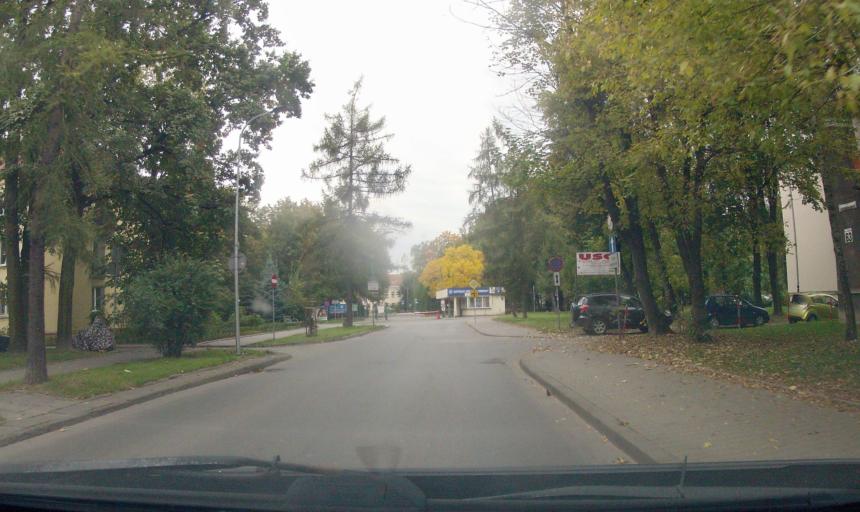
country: PL
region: Lesser Poland Voivodeship
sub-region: Powiat wielicki
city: Kokotow
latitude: 50.0674
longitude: 20.0452
